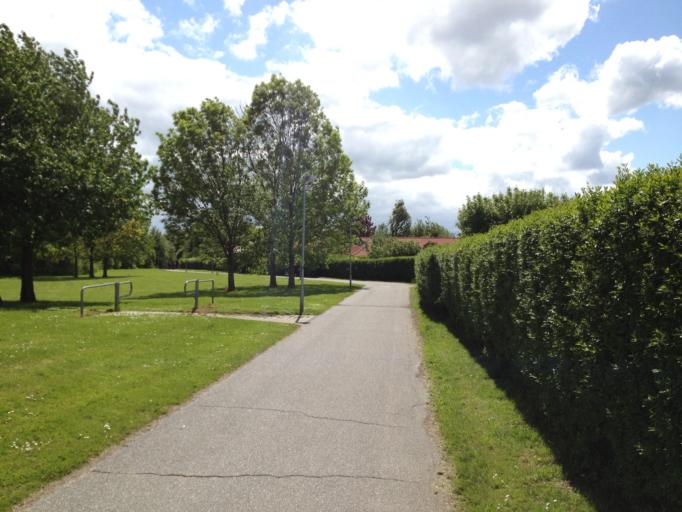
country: DK
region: Capital Region
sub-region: Fredensborg Kommune
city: Niva
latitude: 55.9431
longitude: 12.4957
